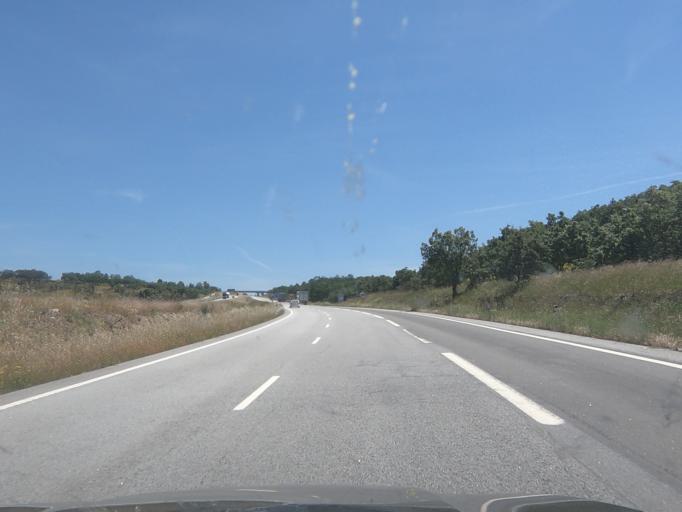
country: PT
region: Guarda
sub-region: Pinhel
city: Pinhel
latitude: 40.6054
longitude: -7.0178
